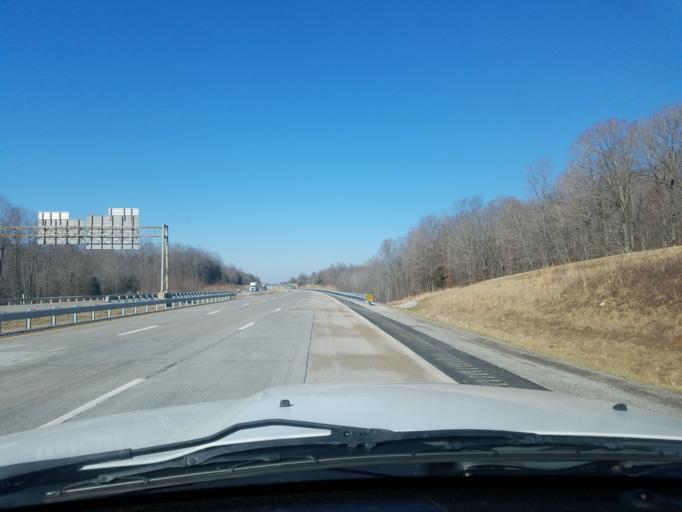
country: US
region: Kentucky
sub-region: Ohio County
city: Beaver Dam
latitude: 37.3888
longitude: -86.8115
